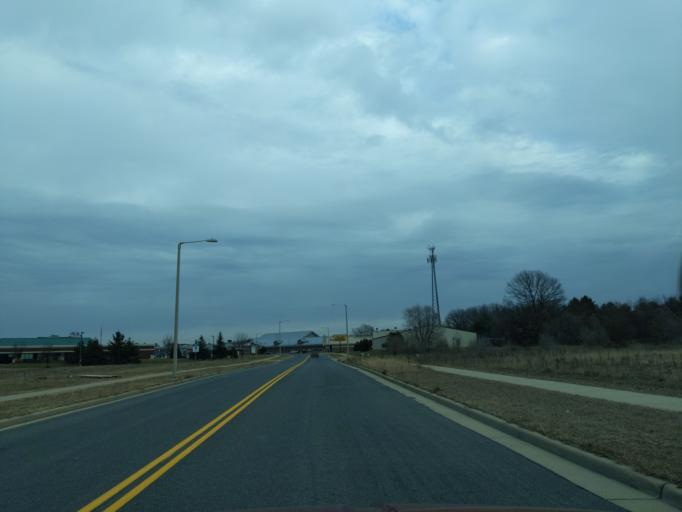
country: US
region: Wisconsin
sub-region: Waushara County
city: Wautoma
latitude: 44.0690
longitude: -89.2751
